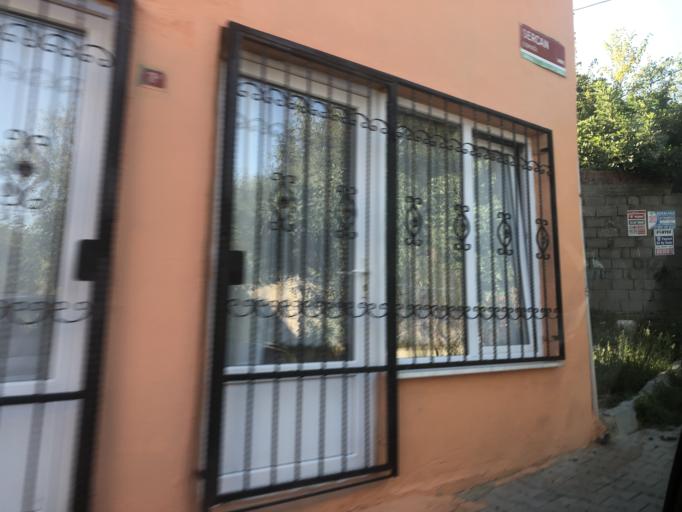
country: TR
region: Istanbul
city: Catalca
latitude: 41.2242
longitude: 28.4764
